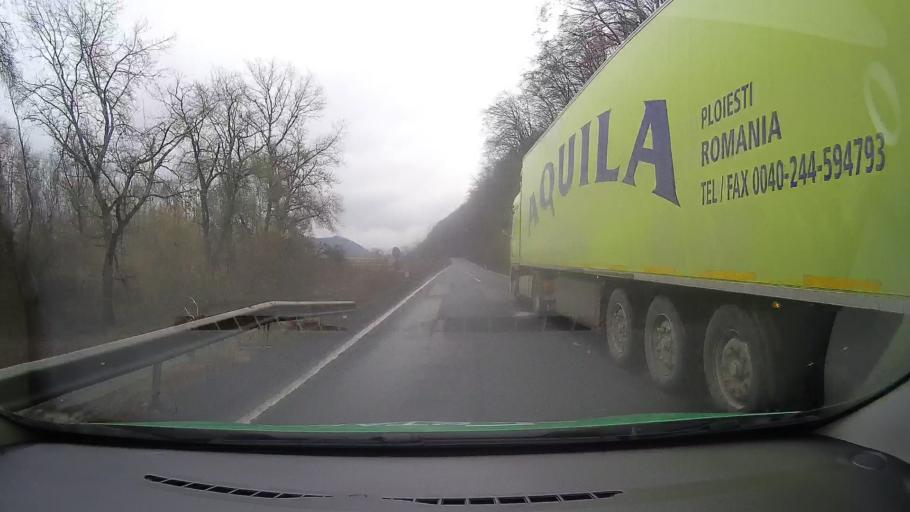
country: RO
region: Hunedoara
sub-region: Comuna Ilia
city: Ilia
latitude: 45.9243
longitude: 22.6859
